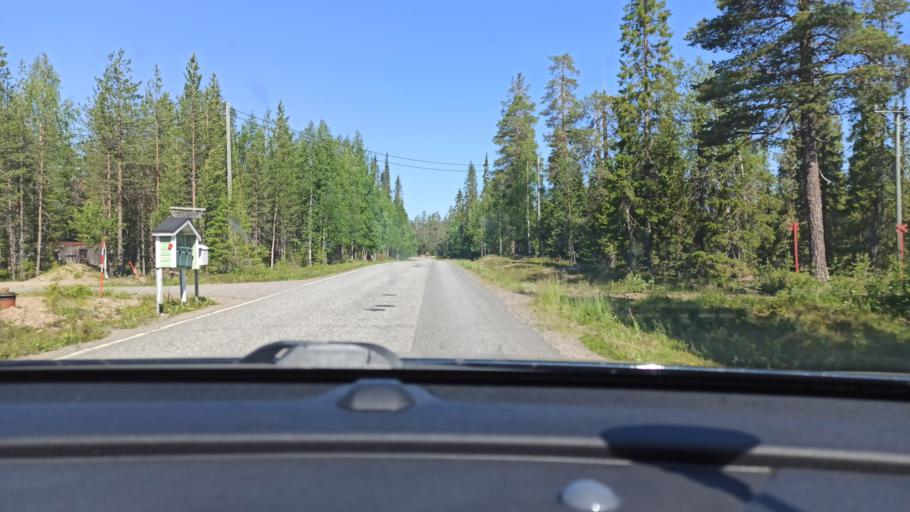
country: FI
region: Lapland
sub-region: Tunturi-Lappi
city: Kolari
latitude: 67.6665
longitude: 24.1604
